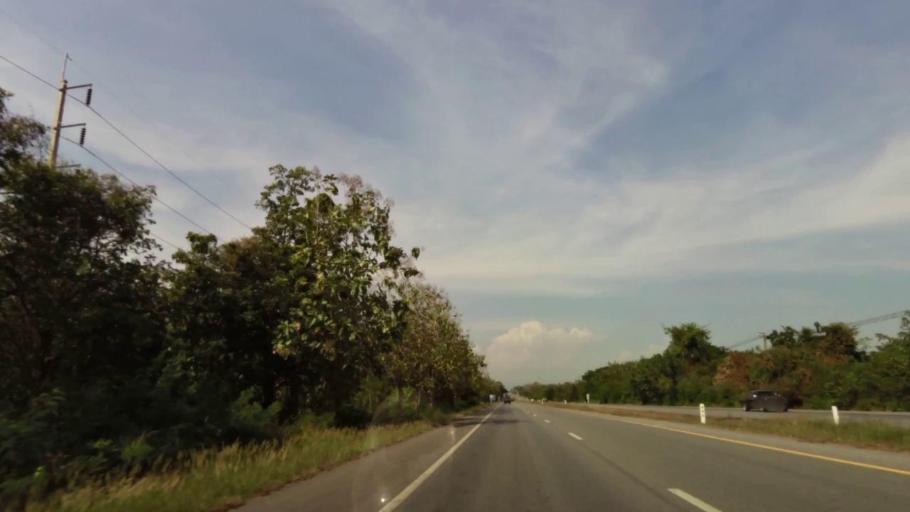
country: TH
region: Uttaradit
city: Tron
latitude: 17.5374
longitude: 100.2028
